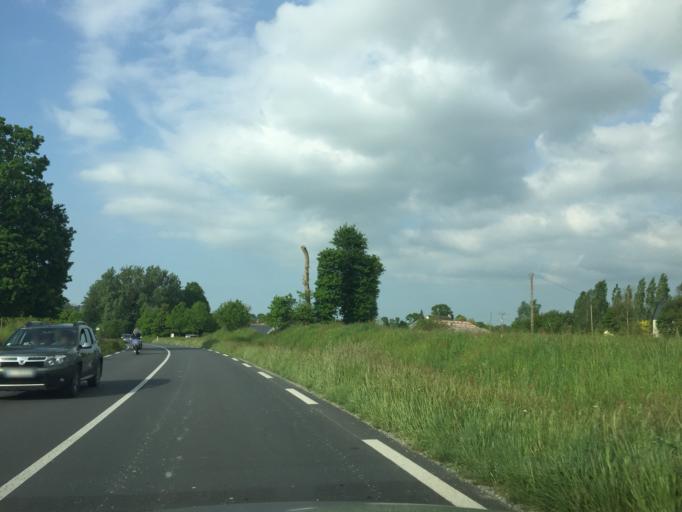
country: FR
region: Brittany
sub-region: Departement des Cotes-d'Armor
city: Caulnes
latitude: 48.3085
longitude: -2.1333
